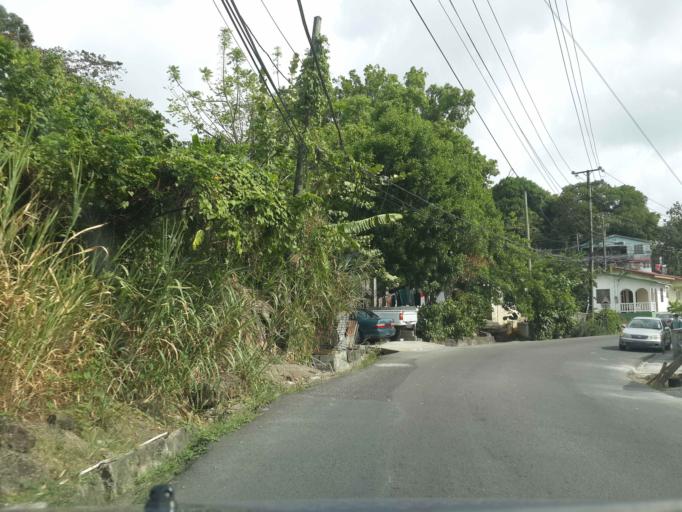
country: LC
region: Castries Quarter
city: Bisee
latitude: 14.0187
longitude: -60.9851
